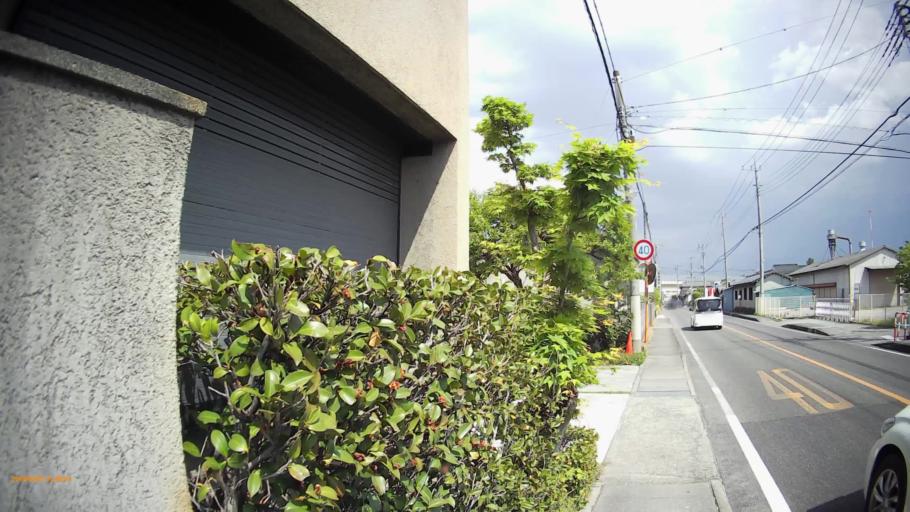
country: JP
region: Yamanashi
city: Ryuo
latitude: 35.6633
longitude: 138.5290
